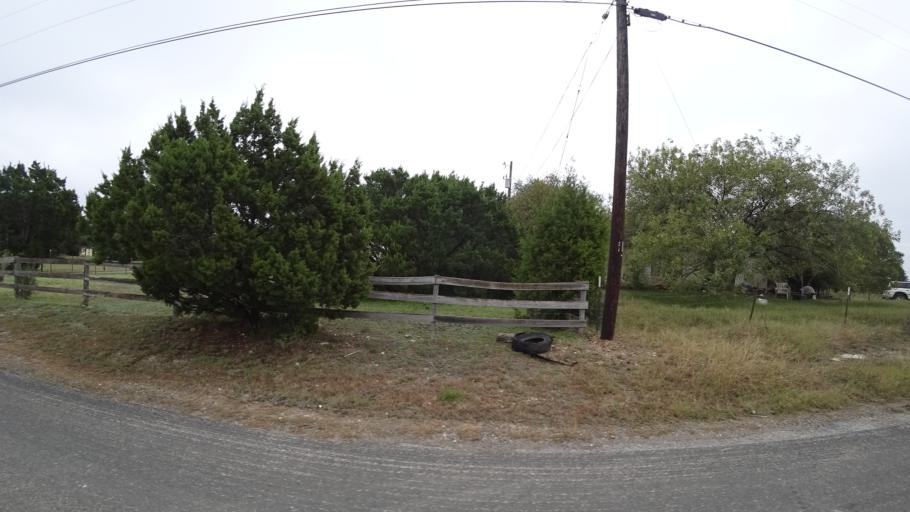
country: US
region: Texas
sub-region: Travis County
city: Barton Creek
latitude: 30.2354
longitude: -97.9081
